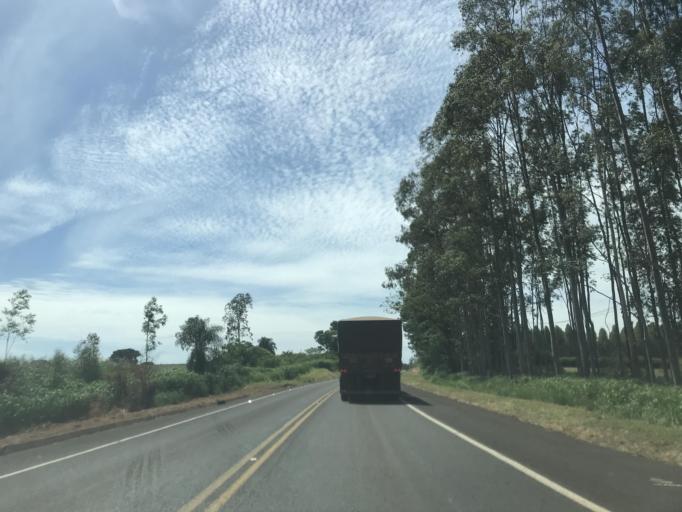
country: BR
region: Parana
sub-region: Paranavai
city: Nova Aurora
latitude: -22.9562
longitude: -52.6626
